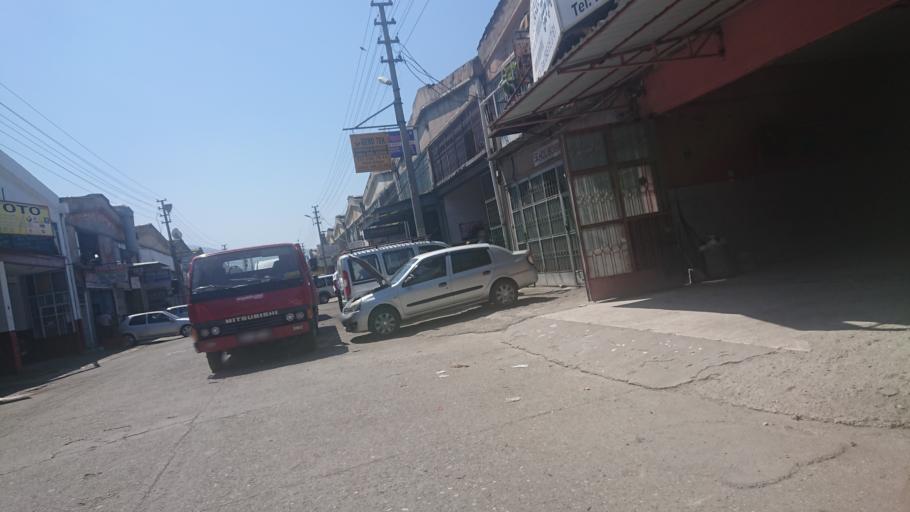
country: TR
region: Samsun
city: Samsun
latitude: 41.2713
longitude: 36.3623
